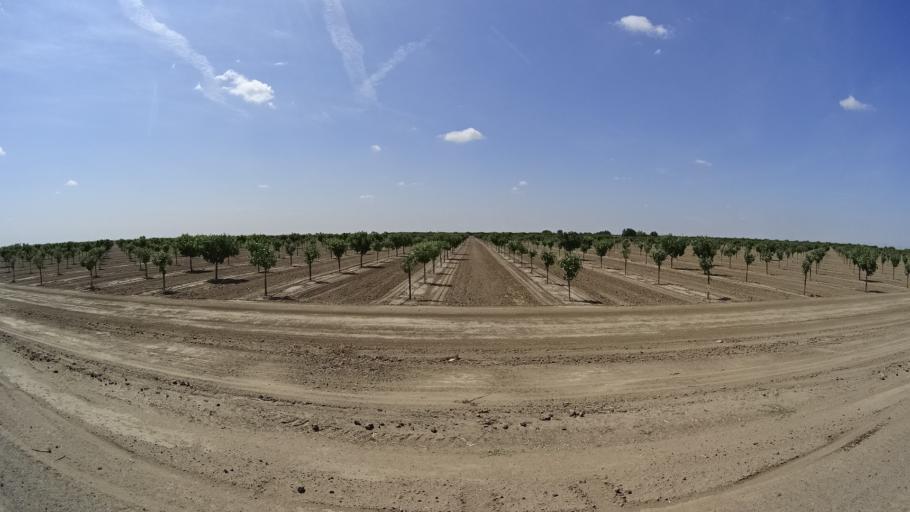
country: US
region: California
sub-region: Kings County
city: Home Garden
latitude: 36.2695
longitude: -119.5584
